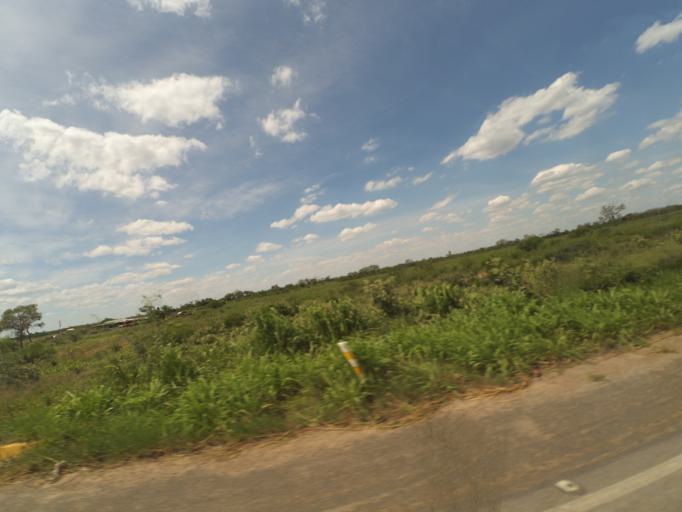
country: BO
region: Santa Cruz
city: Pailon
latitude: -17.5891
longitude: -61.9525
